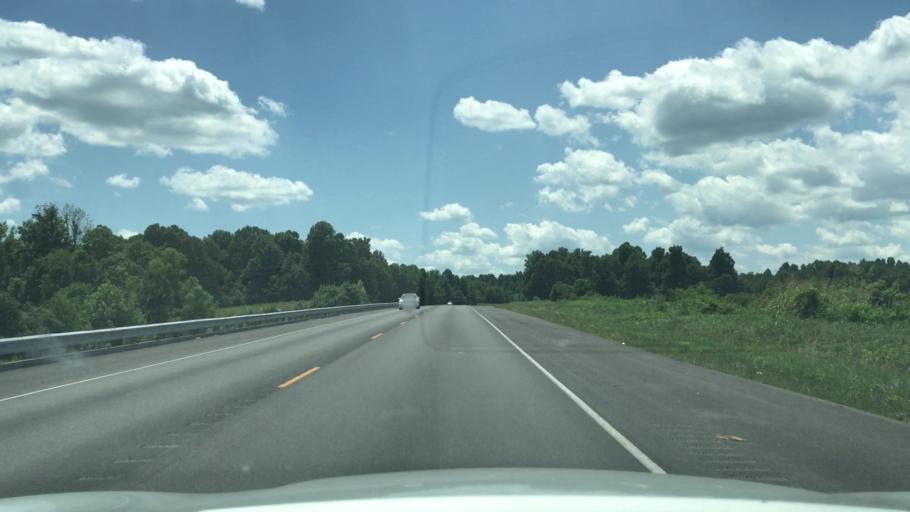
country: US
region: Kentucky
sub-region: Muhlenberg County
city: Greenville
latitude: 37.2086
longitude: -87.1942
